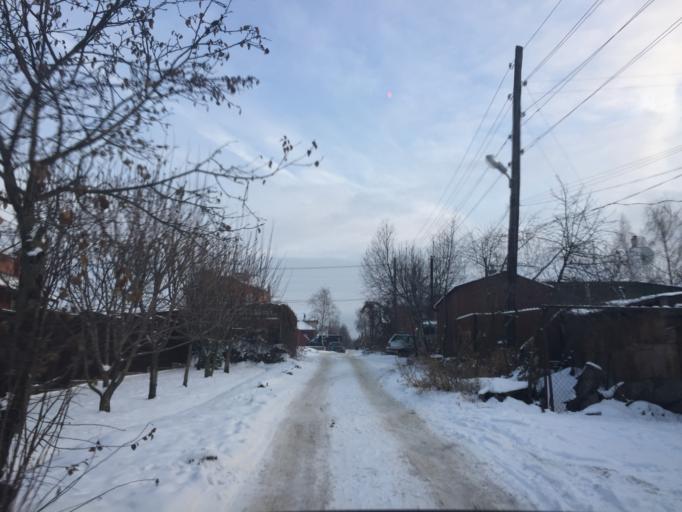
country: RU
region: Tula
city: Tula
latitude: 54.2021
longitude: 37.6771
